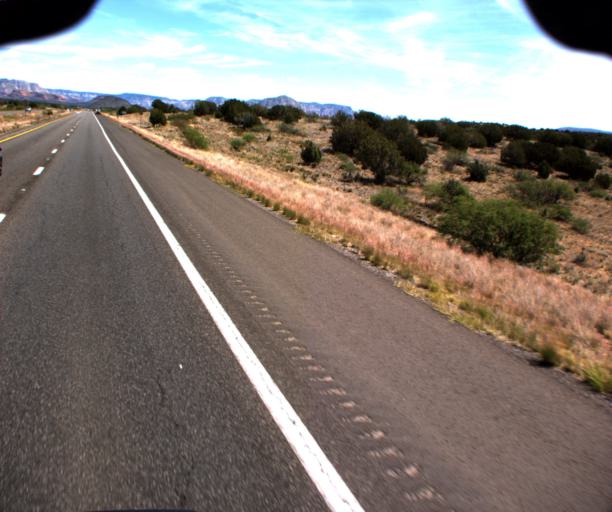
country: US
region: Arizona
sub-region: Yavapai County
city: Cornville
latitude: 34.8105
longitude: -111.9073
